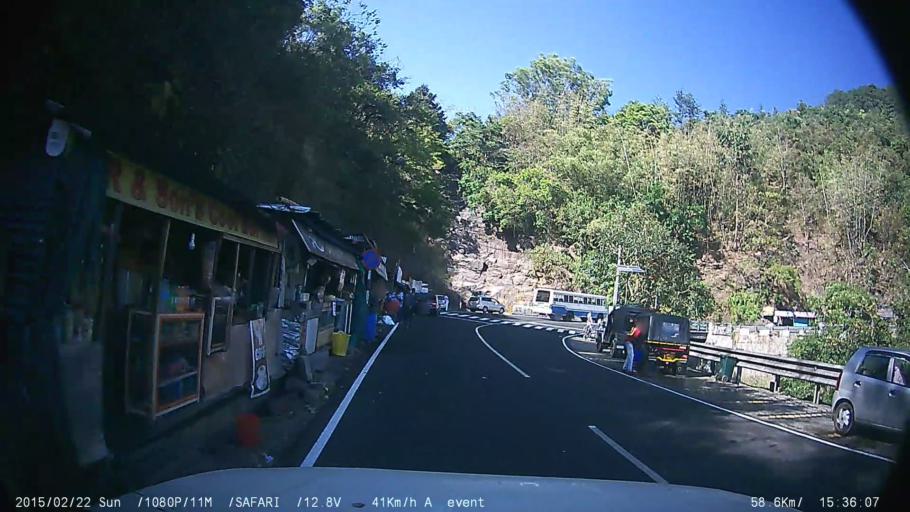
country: IN
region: Kerala
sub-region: Kottayam
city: Erattupetta
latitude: 9.5620
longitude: 76.9772
